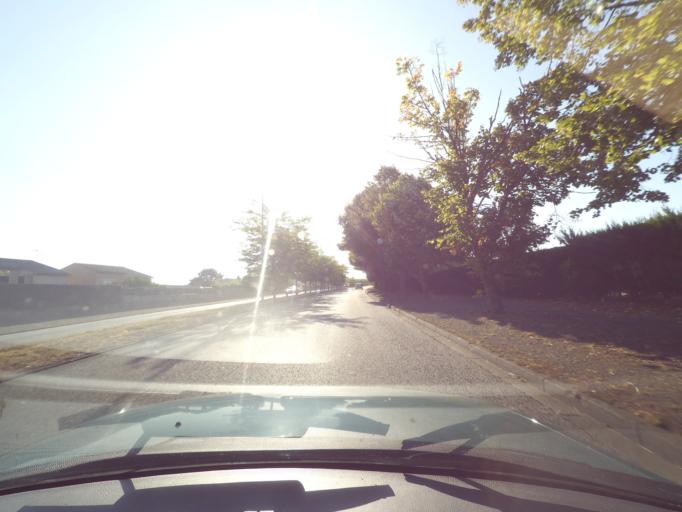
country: FR
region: Poitou-Charentes
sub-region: Departement des Deux-Sevres
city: Chatillon-sur-Thouet
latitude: 46.6535
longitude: -0.2327
